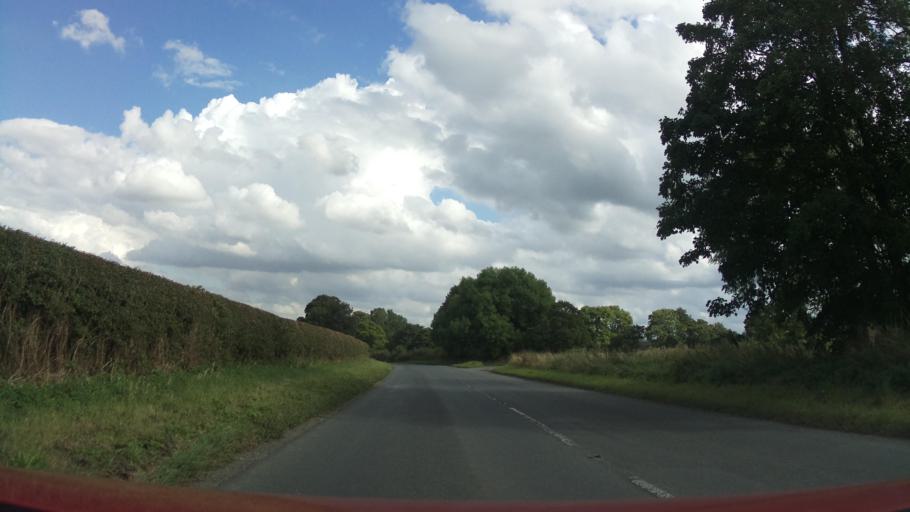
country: GB
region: England
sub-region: North Yorkshire
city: Leyburn
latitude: 54.2687
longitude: -1.7709
